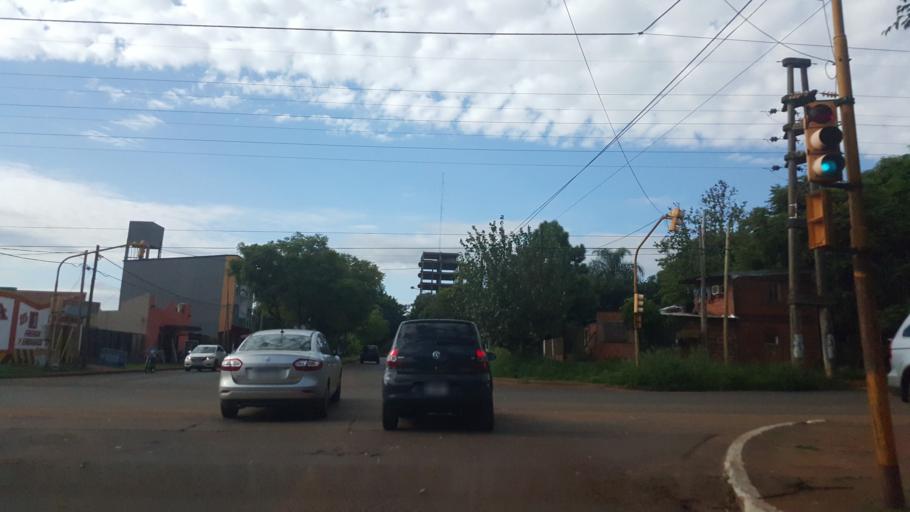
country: AR
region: Misiones
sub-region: Departamento de Capital
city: Posadas
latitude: -27.3742
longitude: -55.9326
